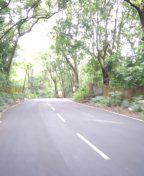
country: IN
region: Kerala
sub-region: Thrissur District
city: Trichur
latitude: 10.5342
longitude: 76.3408
